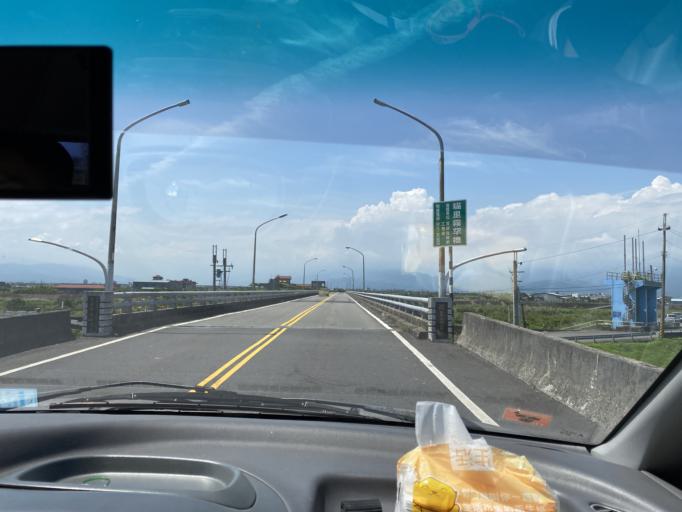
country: TW
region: Taiwan
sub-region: Yilan
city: Yilan
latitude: 24.7238
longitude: 121.8189
